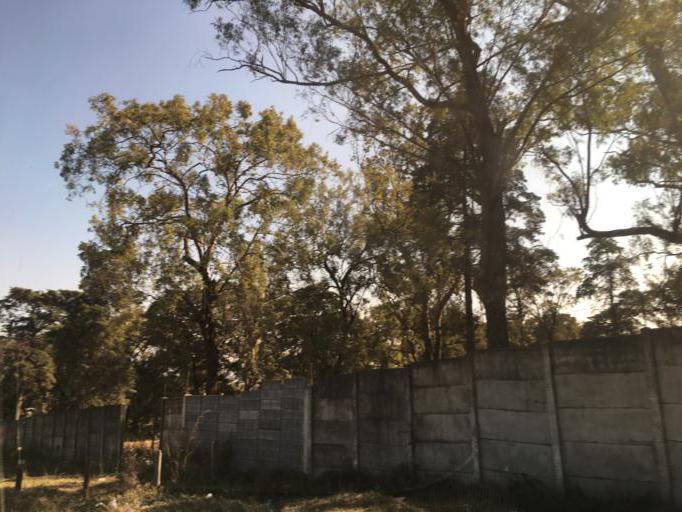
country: GT
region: Guatemala
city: Mixco
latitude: 14.6076
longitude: -90.5754
